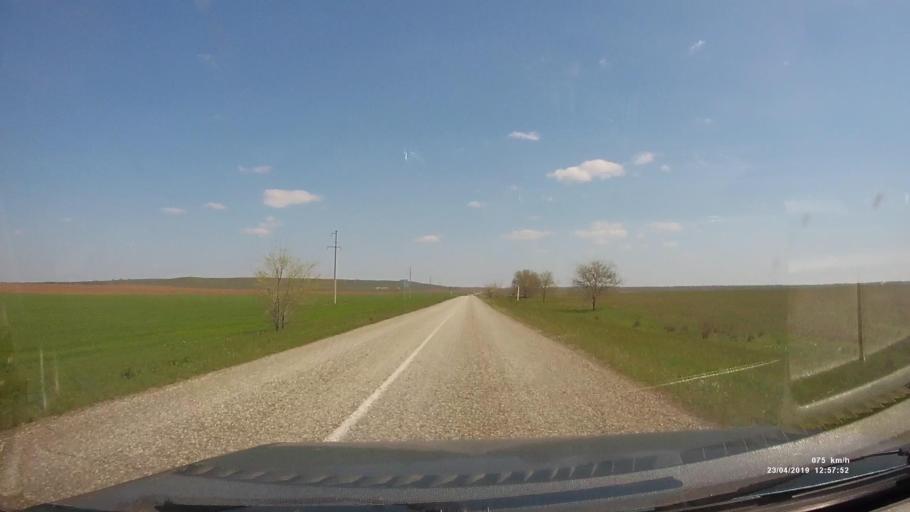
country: RU
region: Kalmykiya
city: Yashalta
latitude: 46.6042
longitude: 42.5864
